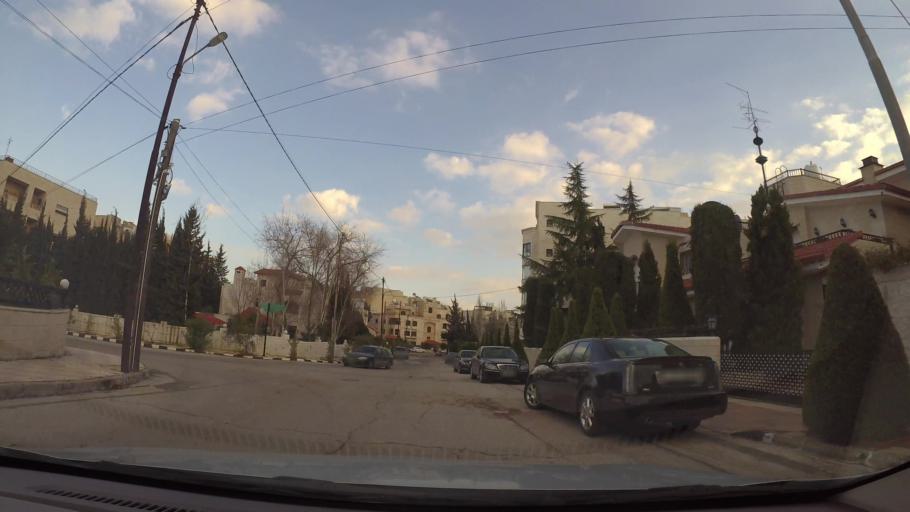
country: JO
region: Amman
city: Al Jubayhah
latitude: 31.9811
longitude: 35.8630
